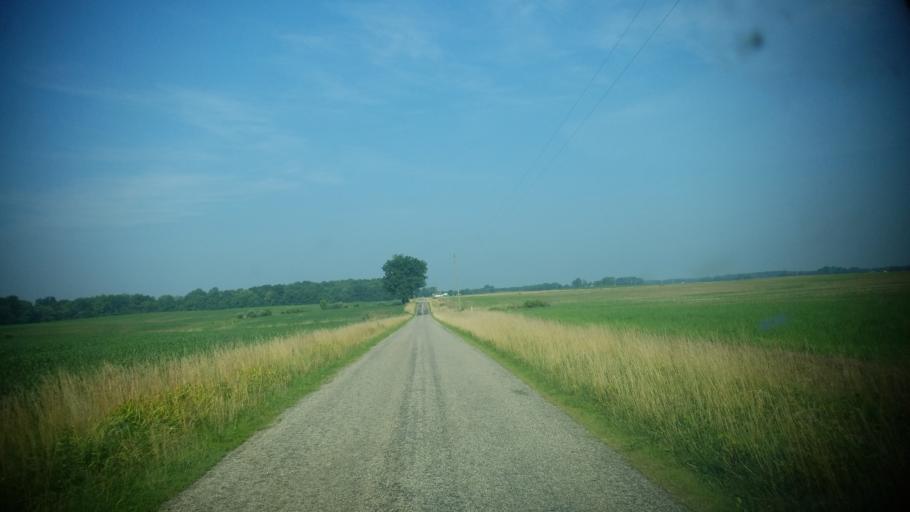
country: US
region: Illinois
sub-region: Clay County
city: Flora
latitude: 38.6030
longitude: -88.4234
